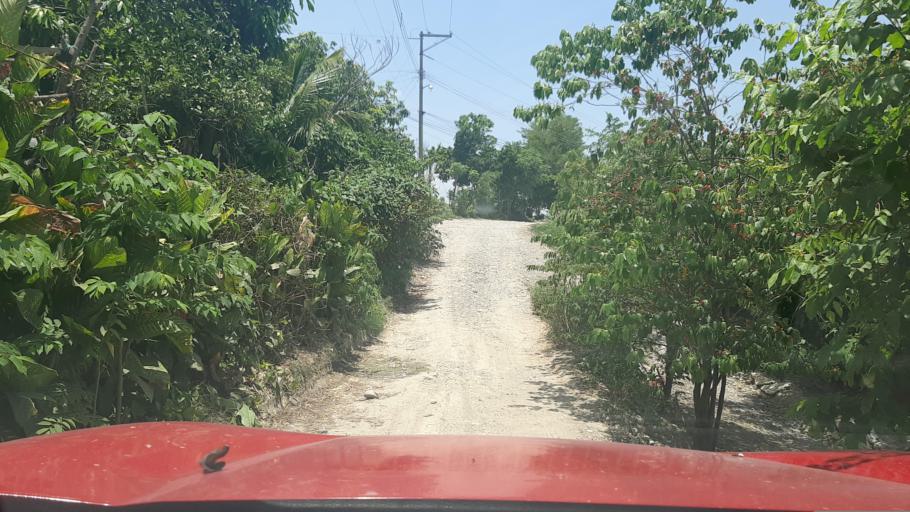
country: MX
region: Veracruz
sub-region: Poza Rica de Hidalgo
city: Arroyo del Maiz Uno
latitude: 20.4980
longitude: -97.4213
